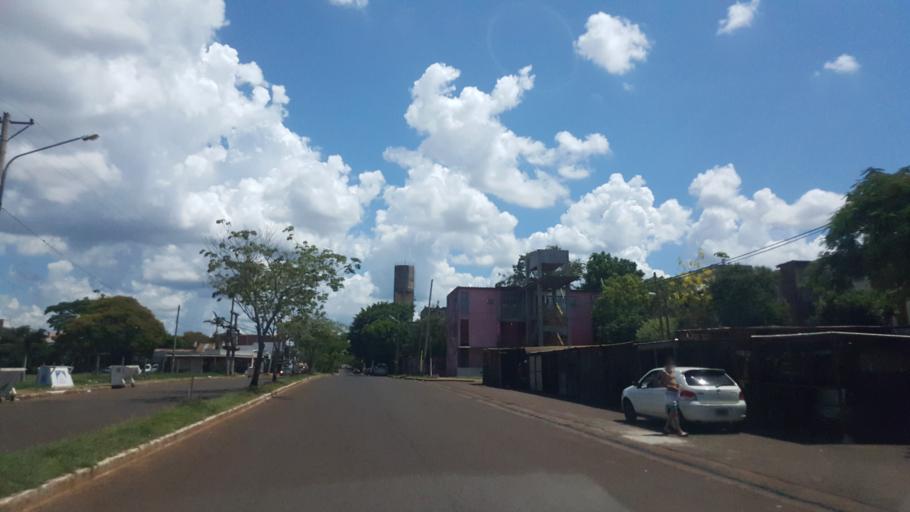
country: AR
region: Misiones
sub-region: Departamento de Capital
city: Posadas
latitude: -27.3636
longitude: -55.9464
